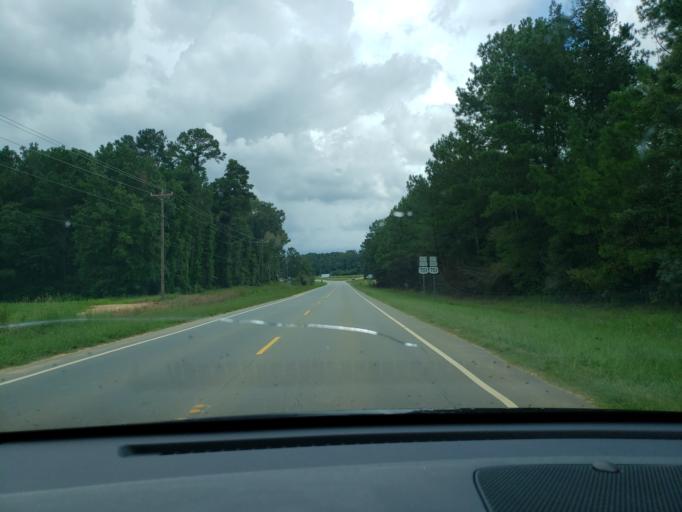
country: US
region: North Carolina
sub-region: Columbus County
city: Whiteville
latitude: 34.4659
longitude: -78.6733
